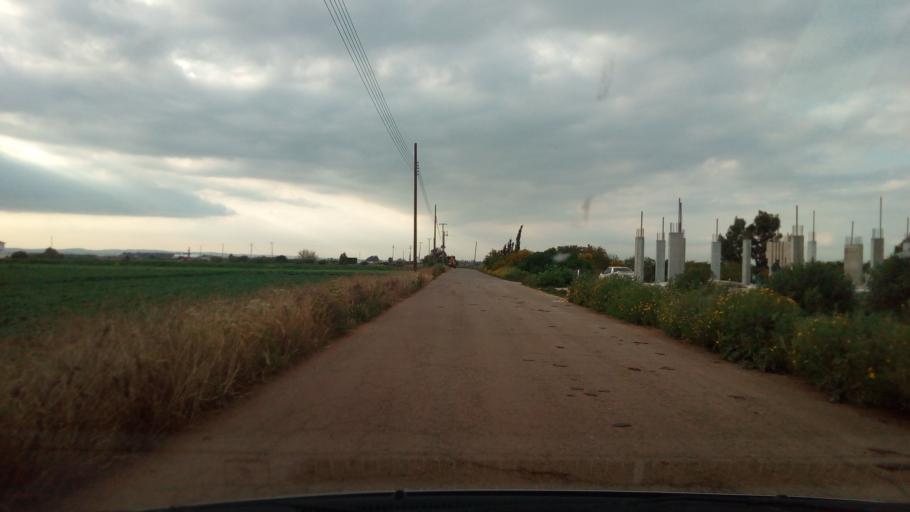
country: CY
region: Ammochostos
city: Avgorou
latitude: 34.9867
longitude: 33.8336
